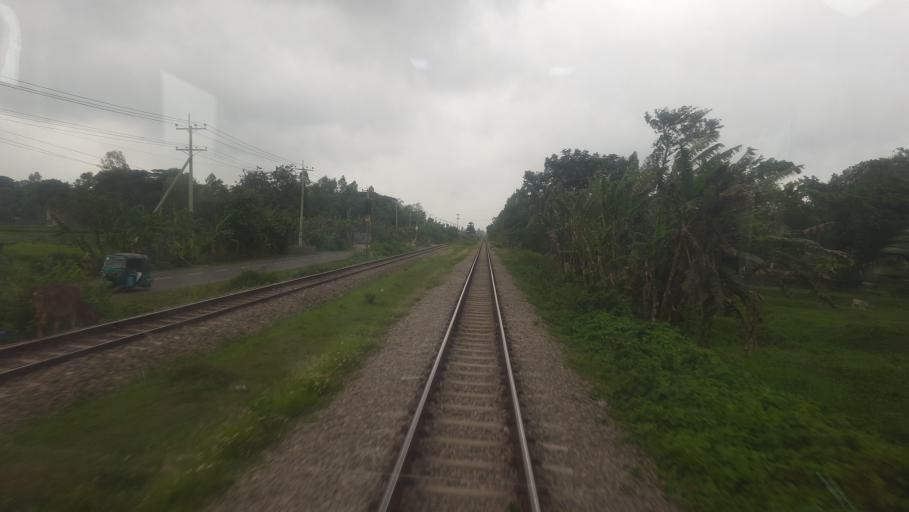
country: BD
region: Dhaka
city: Narsingdi
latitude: 23.9602
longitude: 90.8076
